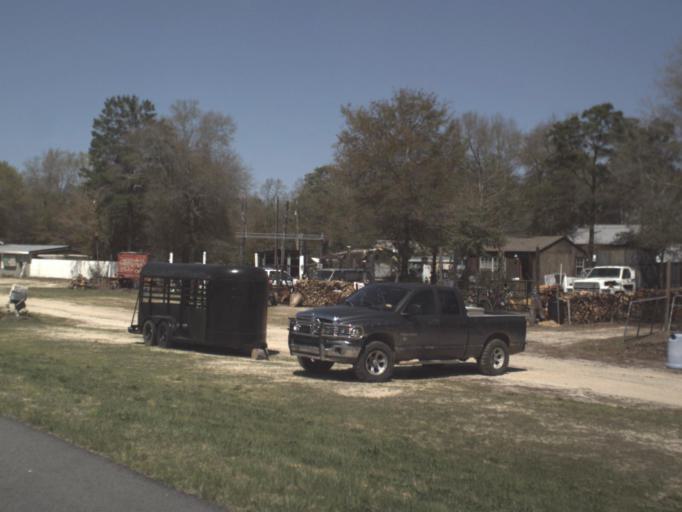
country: US
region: Florida
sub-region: Walton County
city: DeFuniak Springs
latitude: 30.7490
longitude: -86.2423
